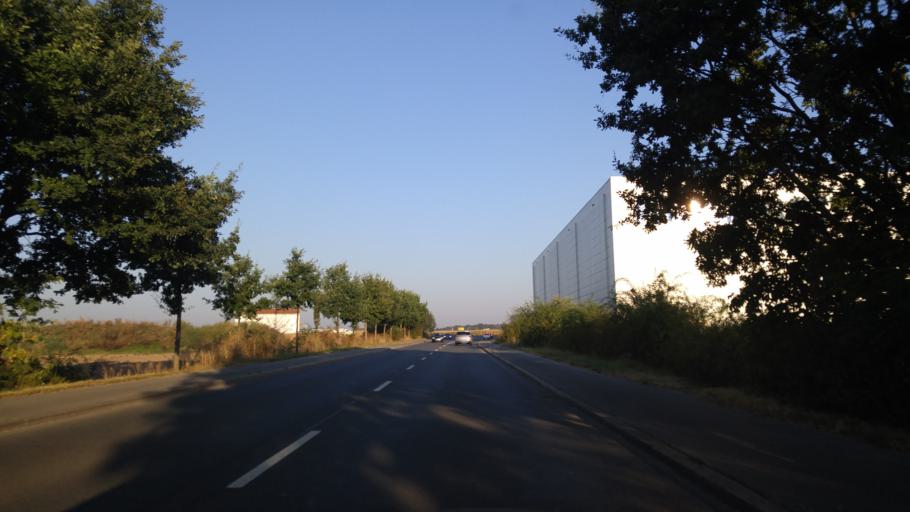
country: DE
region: Bavaria
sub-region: Regierungsbezirk Mittelfranken
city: Furth
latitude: 49.4974
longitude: 10.9462
